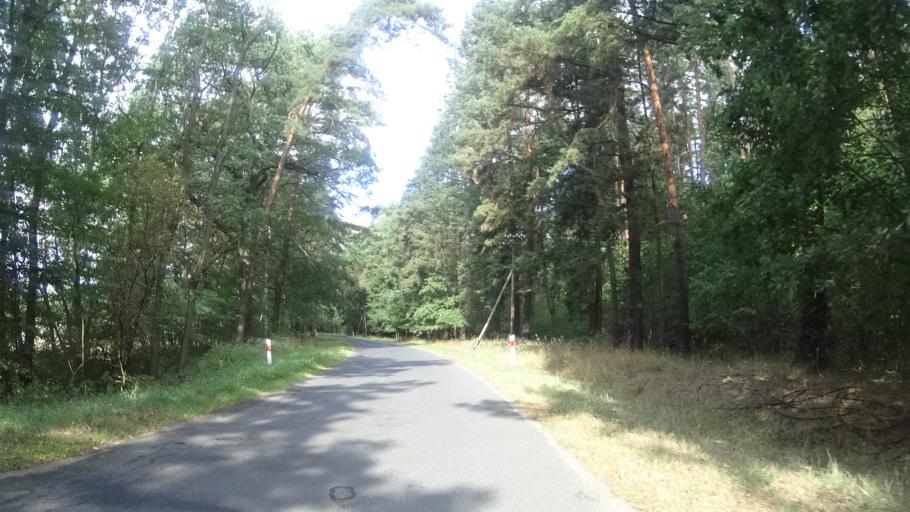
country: PL
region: Lubusz
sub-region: Powiat zarski
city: Przewoz
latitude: 51.4901
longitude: 14.8870
